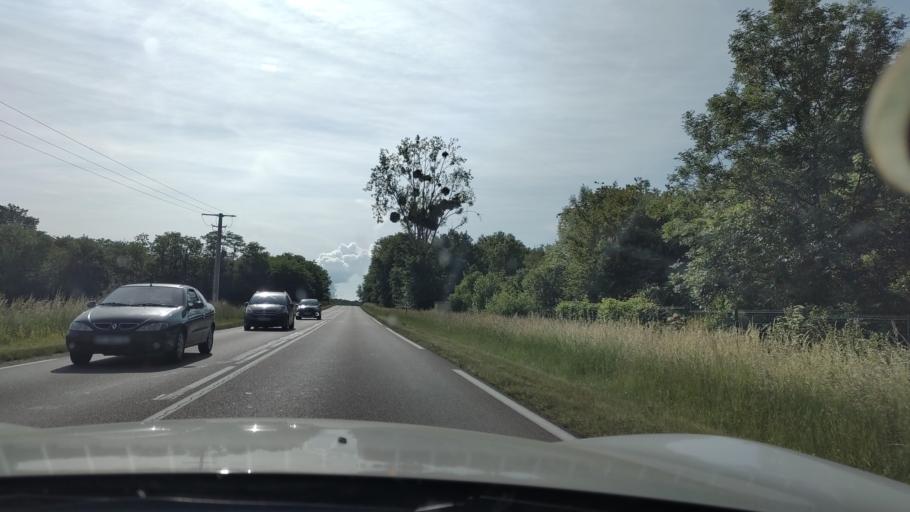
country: FR
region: Ile-de-France
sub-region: Departement de Seine-et-Marne
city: Sourdun
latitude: 48.5330
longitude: 3.3762
